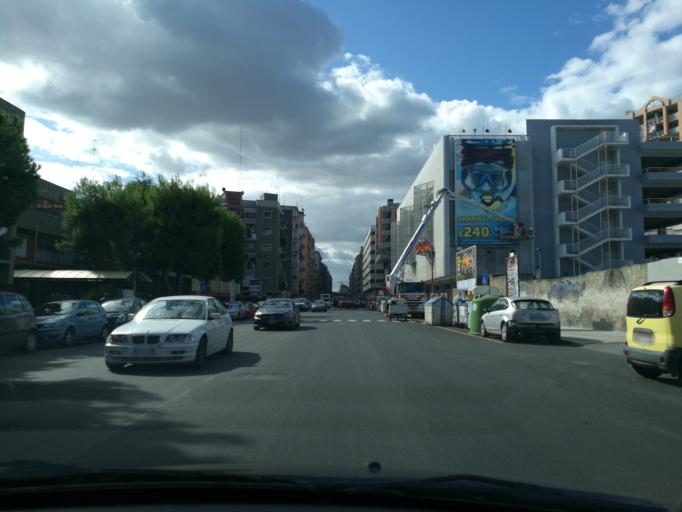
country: IT
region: Apulia
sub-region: Provincia di Bari
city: Bari
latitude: 41.1243
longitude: 16.8518
